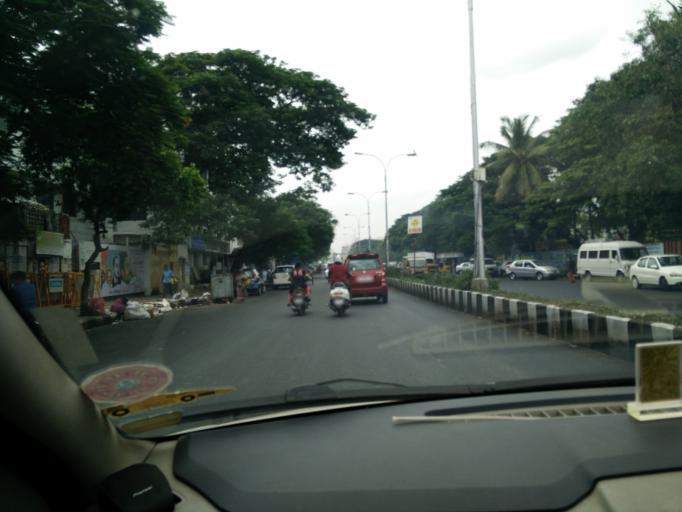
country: IN
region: Tamil Nadu
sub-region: Chennai
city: Chennai
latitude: 13.0741
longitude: 80.2763
